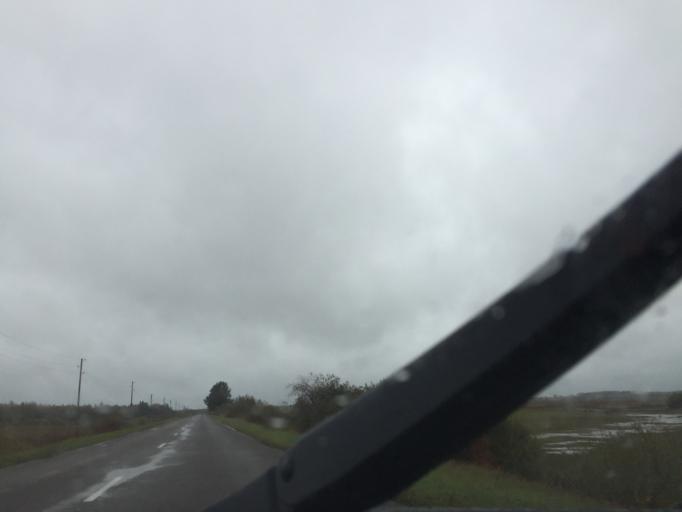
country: LV
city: Tireli
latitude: 56.8174
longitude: 23.5708
